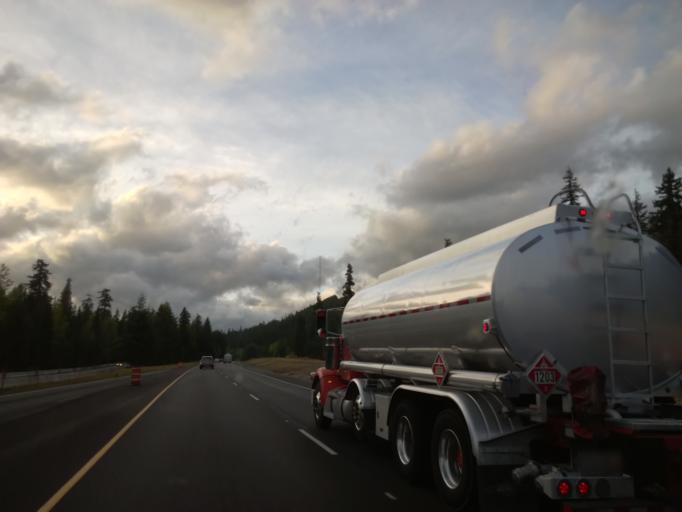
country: US
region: Washington
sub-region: Kittitas County
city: Cle Elum
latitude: 47.3194
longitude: -121.3217
